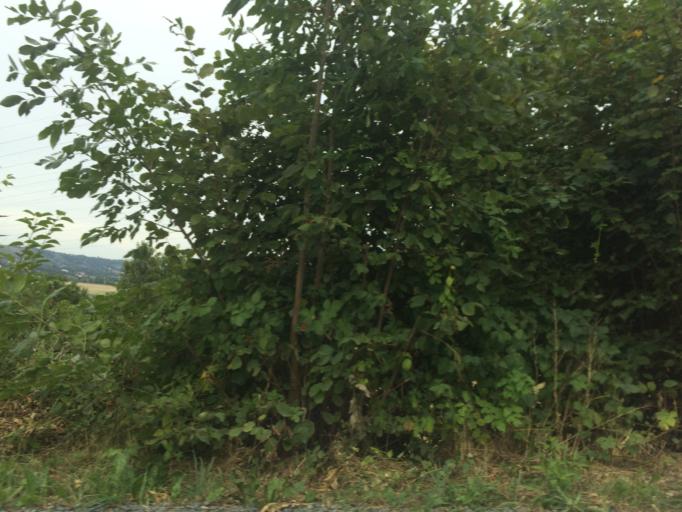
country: DE
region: Saxony
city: Coswig
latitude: 51.0897
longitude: 13.6043
